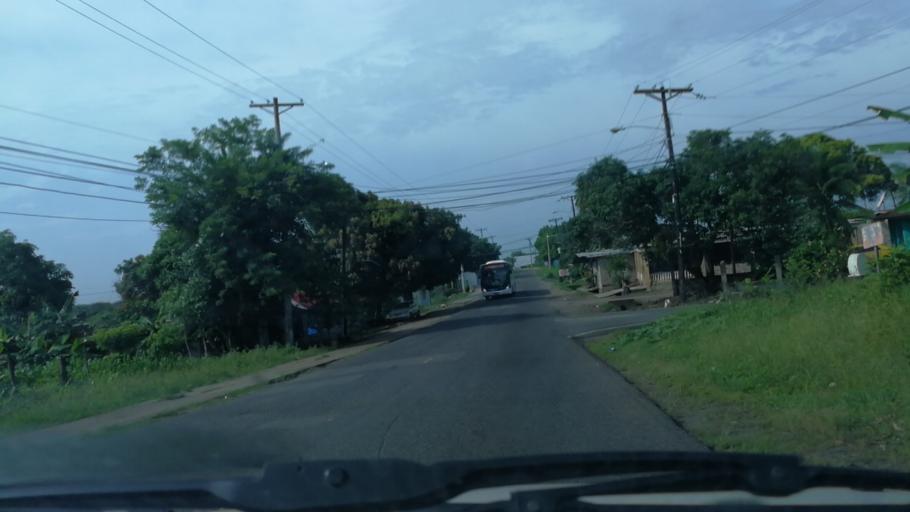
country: PA
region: Panama
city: Pacora
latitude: 9.0917
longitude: -79.2885
